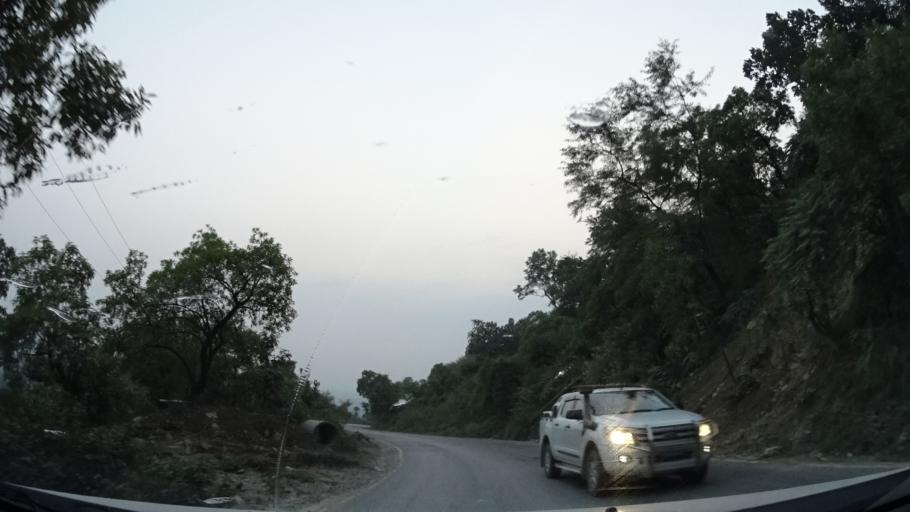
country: IN
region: Uttar Pradesh
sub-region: Maharajganj
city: Nichlaul
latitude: 27.5513
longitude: 83.8094
